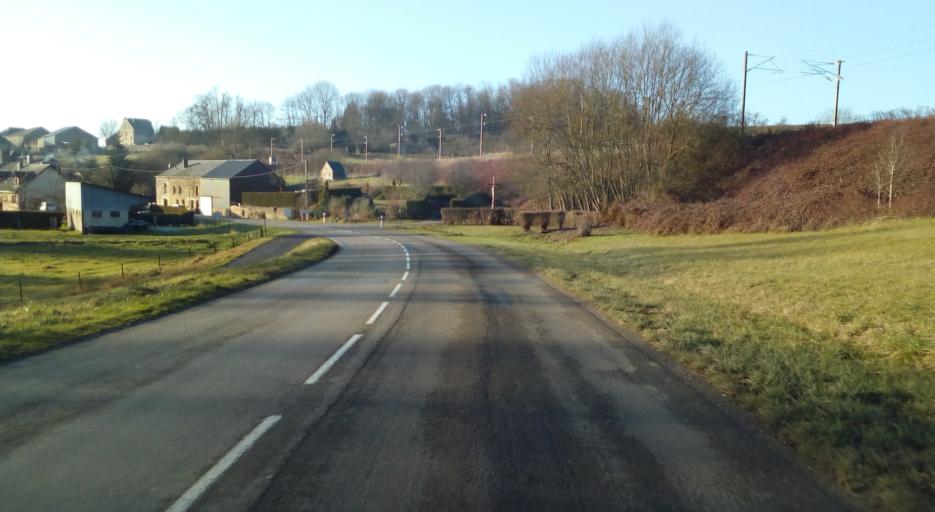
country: FR
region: Champagne-Ardenne
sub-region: Departement des Ardennes
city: Rimogne
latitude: 49.7776
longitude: 4.4420
